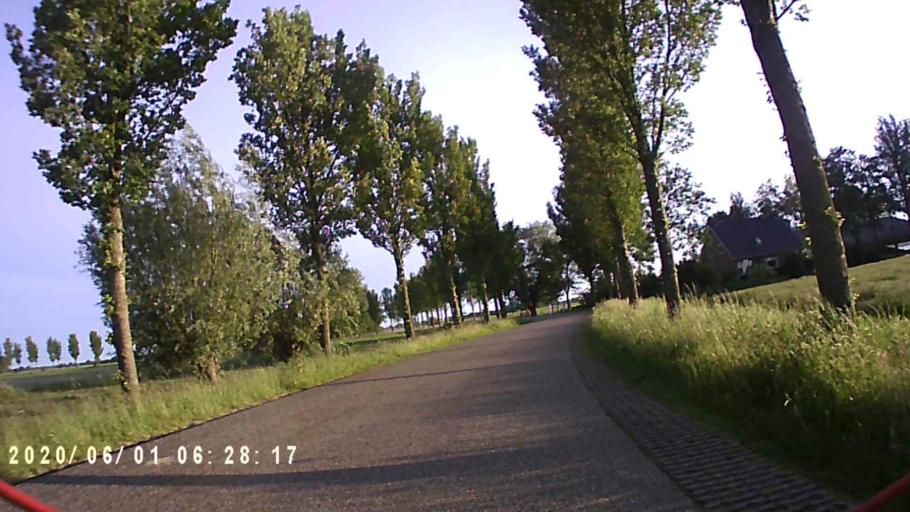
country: NL
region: Friesland
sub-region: Gemeente Kollumerland en Nieuwkruisland
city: Kollum
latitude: 53.2711
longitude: 6.1939
